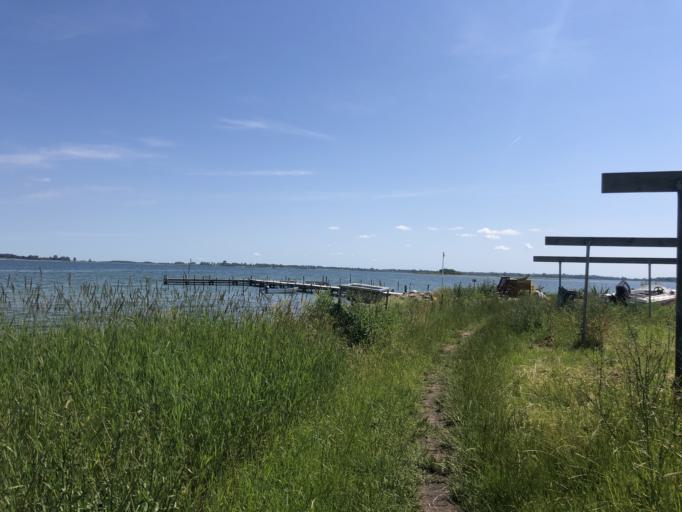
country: DK
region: South Denmark
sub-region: AEro Kommune
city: AEroskobing
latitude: 54.8857
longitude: 10.4168
